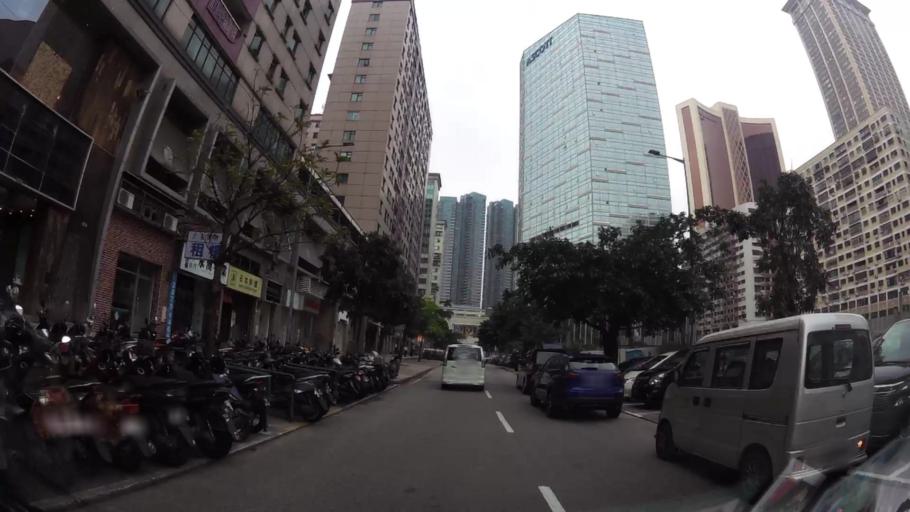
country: MO
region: Macau
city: Macau
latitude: 22.1872
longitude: 113.5508
